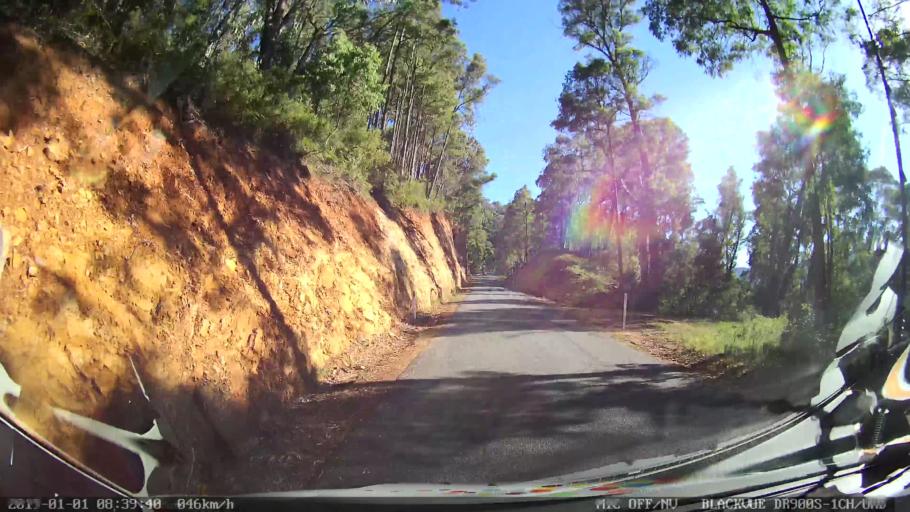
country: AU
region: New South Wales
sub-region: Snowy River
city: Jindabyne
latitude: -36.3298
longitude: 148.1932
